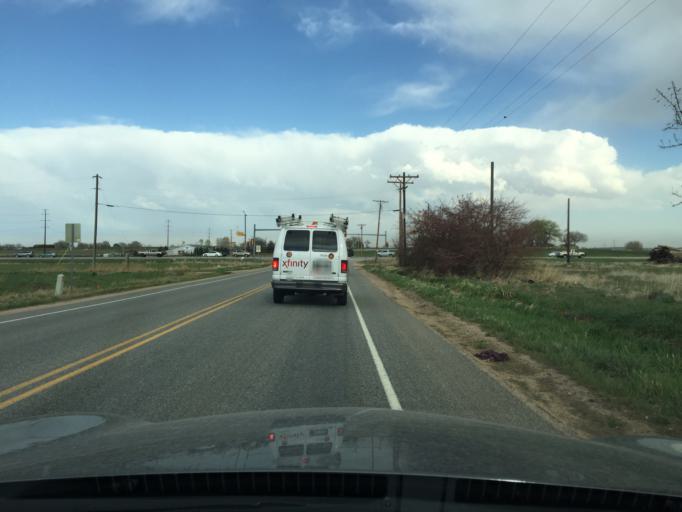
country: US
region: Colorado
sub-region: Boulder County
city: Erie
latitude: 40.0729
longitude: -105.1044
